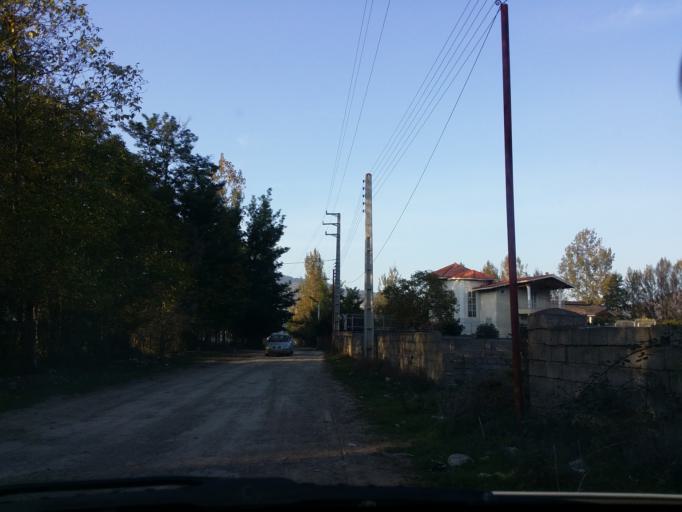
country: IR
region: Mazandaran
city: `Abbasabad
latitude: 36.5120
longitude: 51.1900
